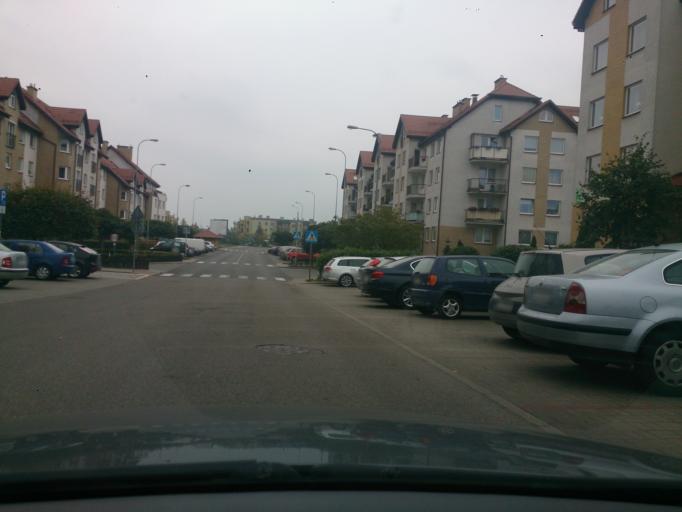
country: PL
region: Pomeranian Voivodeship
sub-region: Gdynia
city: Wielki Kack
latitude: 54.4664
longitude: 18.4861
